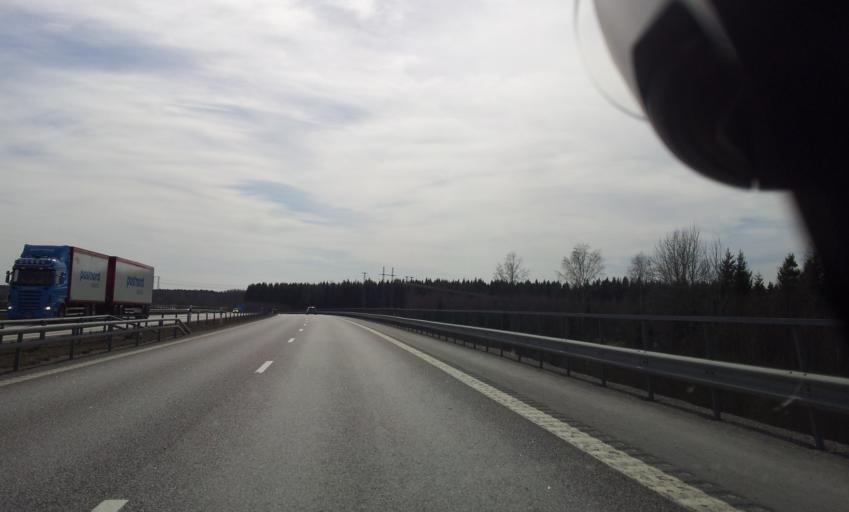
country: SE
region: Uppsala
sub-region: Tierps Kommun
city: Tierp
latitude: 60.3608
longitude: 17.4745
